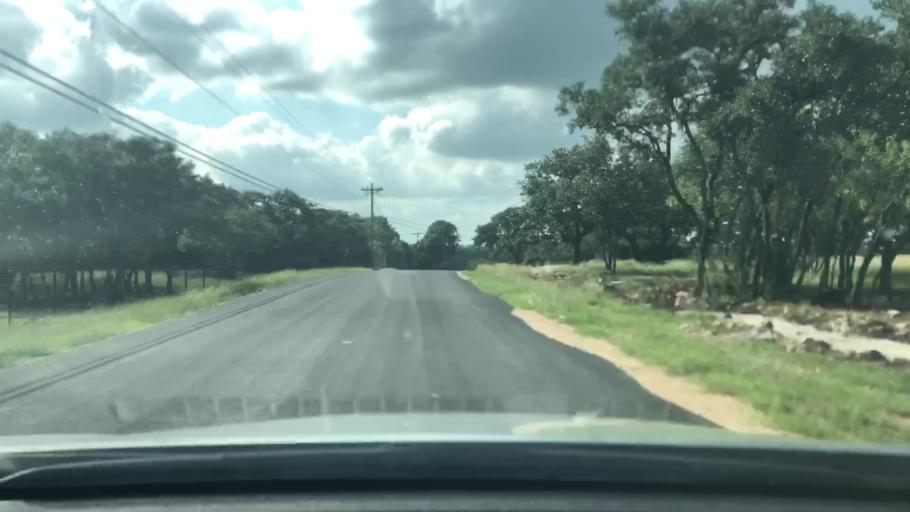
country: US
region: Texas
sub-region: Bexar County
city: Fair Oaks Ranch
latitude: 29.7676
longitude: -98.6287
